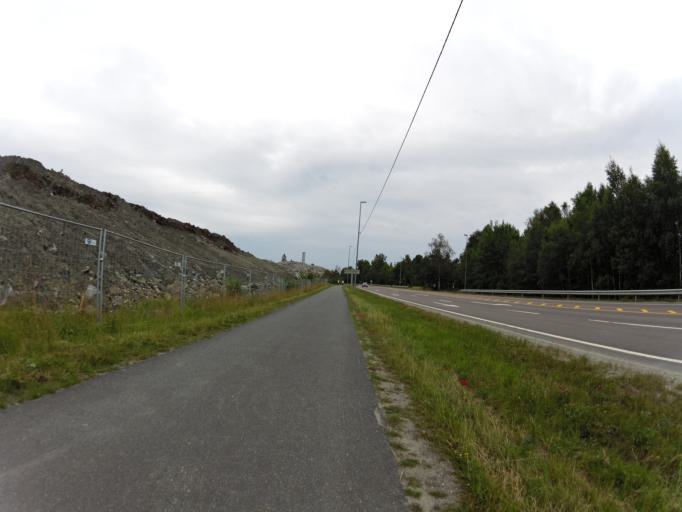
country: NO
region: Akershus
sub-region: Vestby
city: Vestby
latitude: 59.5788
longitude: 10.7382
